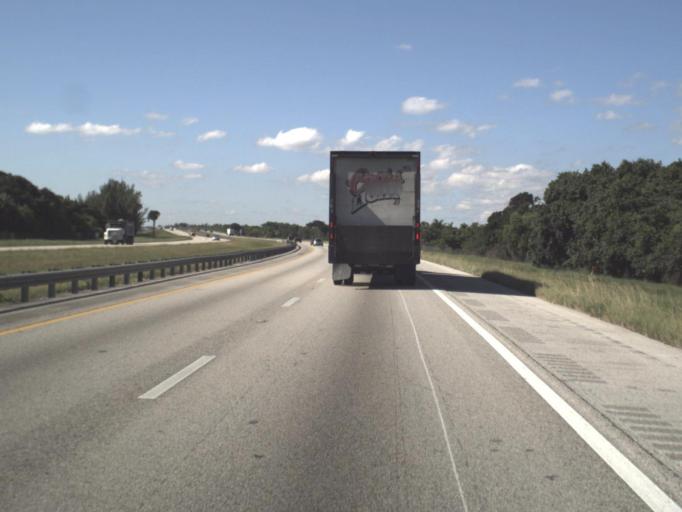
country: US
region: Florida
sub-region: Miami-Dade County
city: Country Club
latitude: 25.9691
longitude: -80.3258
